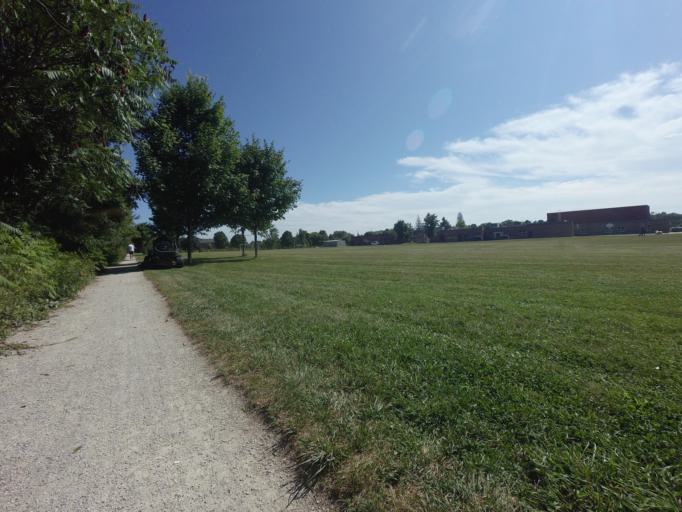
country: CA
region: Ontario
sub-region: Wellington County
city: Guelph
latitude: 43.6885
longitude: -80.4213
